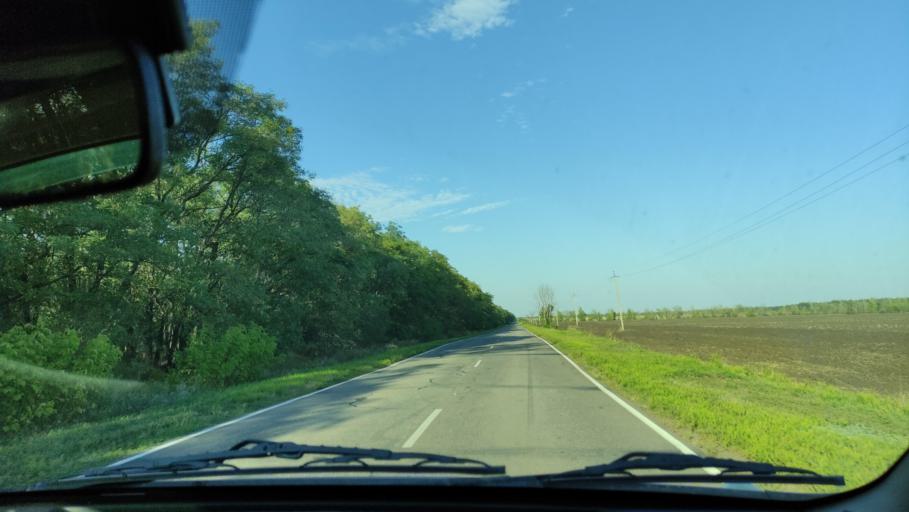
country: RU
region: Voronezj
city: Verkhniy Mamon
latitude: 50.1263
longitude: 40.3155
